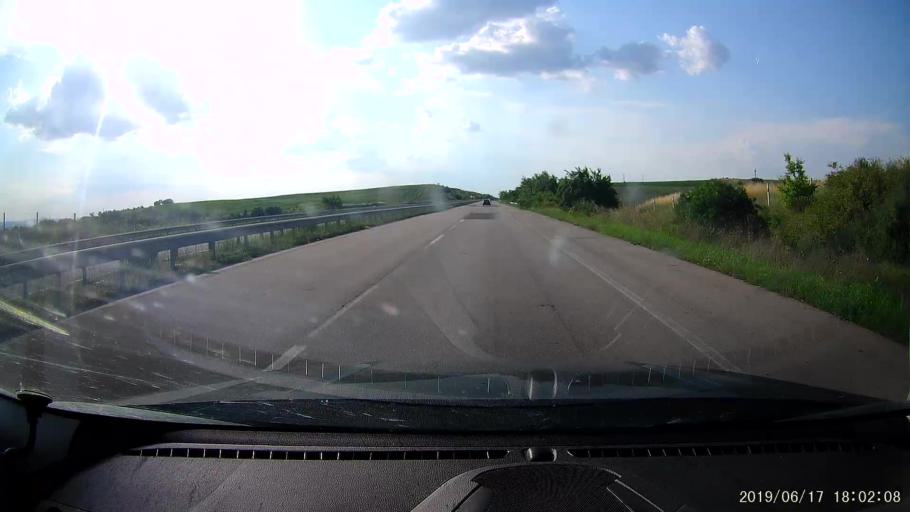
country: BG
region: Khaskovo
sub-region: Obshtina Svilengrad
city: Svilengrad
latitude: 41.7543
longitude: 26.2368
